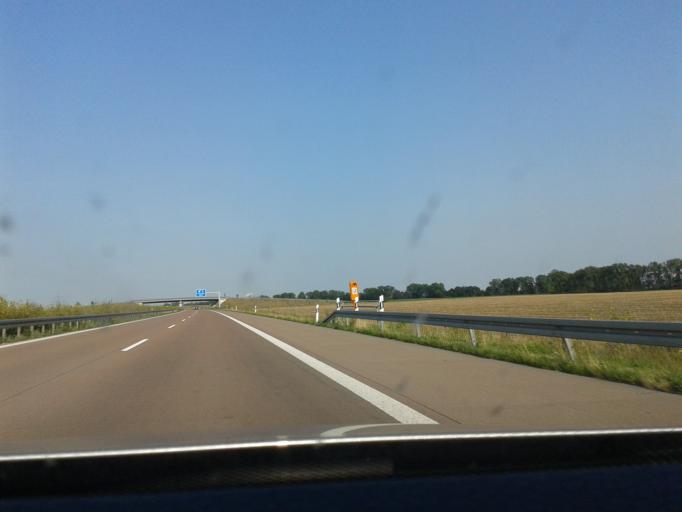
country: DE
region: Saxony-Anhalt
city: Schafstadt
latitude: 51.3994
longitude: 11.7460
